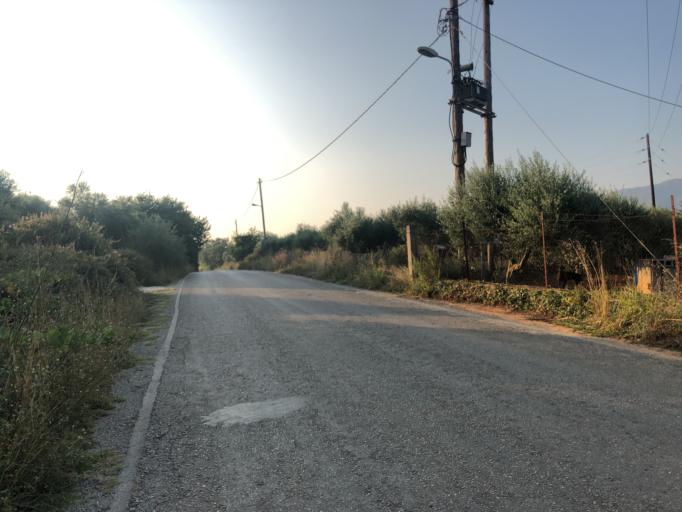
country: GR
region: Crete
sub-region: Nomos Chanias
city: Georgioupolis
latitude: 35.3511
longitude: 24.2770
